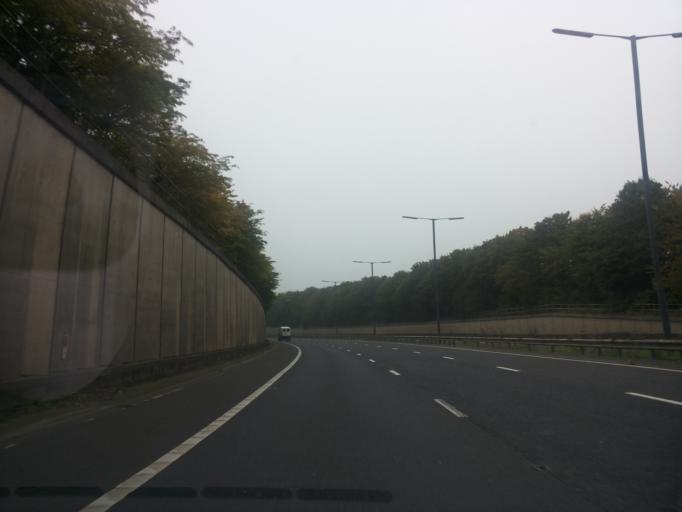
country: GB
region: England
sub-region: Borough of Tameside
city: Denton
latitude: 53.4585
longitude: -2.1094
